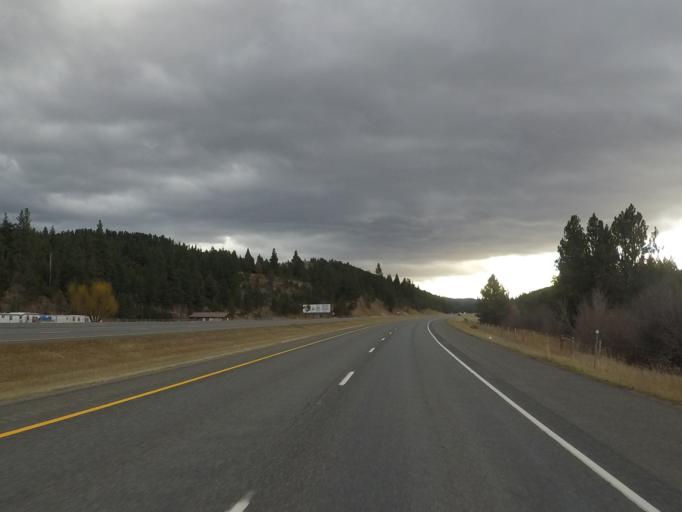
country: US
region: Montana
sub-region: Jefferson County
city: Clancy
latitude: 46.4493
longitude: -111.9872
